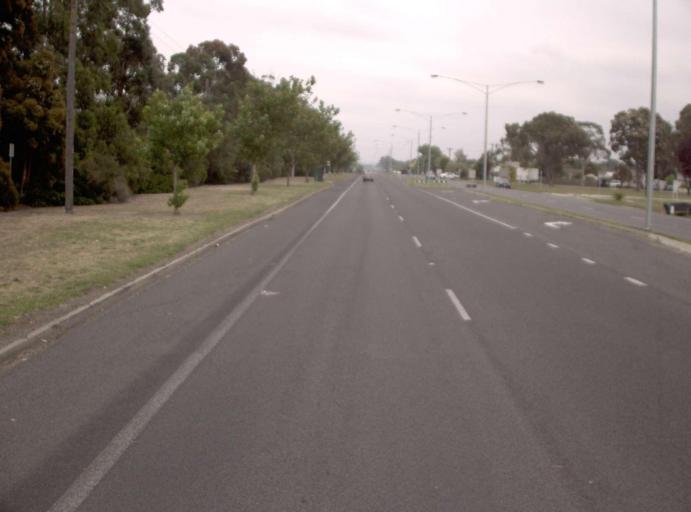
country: AU
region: Victoria
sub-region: Latrobe
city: Traralgon
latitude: -38.2025
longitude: 146.5221
